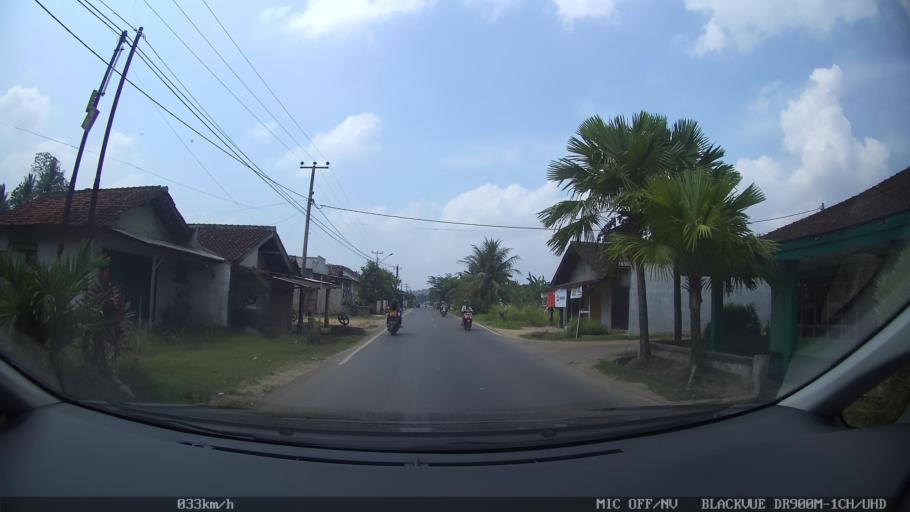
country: ID
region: Lampung
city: Pringsewu
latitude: -5.3741
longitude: 104.9662
